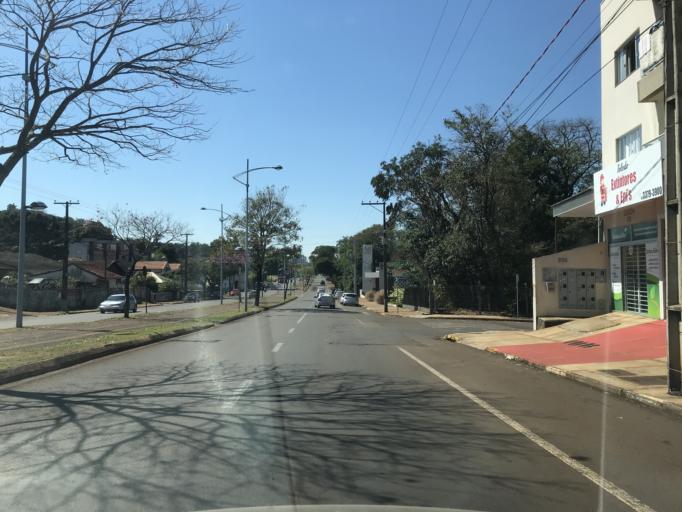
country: BR
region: Parana
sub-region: Toledo
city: Toledo
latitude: -24.7266
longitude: -53.7352
